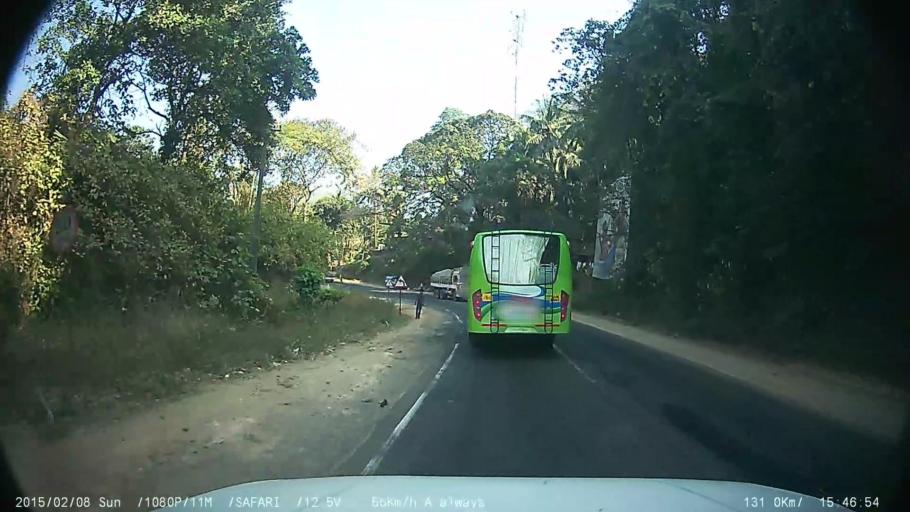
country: IN
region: Kerala
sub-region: Thrissur District
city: Chelakara
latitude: 10.5730
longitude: 76.3850
